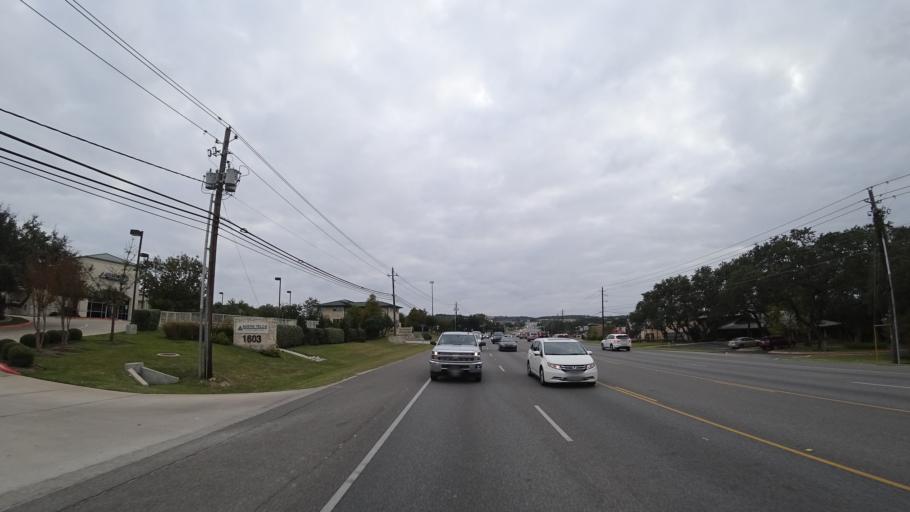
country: US
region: Texas
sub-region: Travis County
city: The Hills
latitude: 30.3473
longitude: -97.9641
